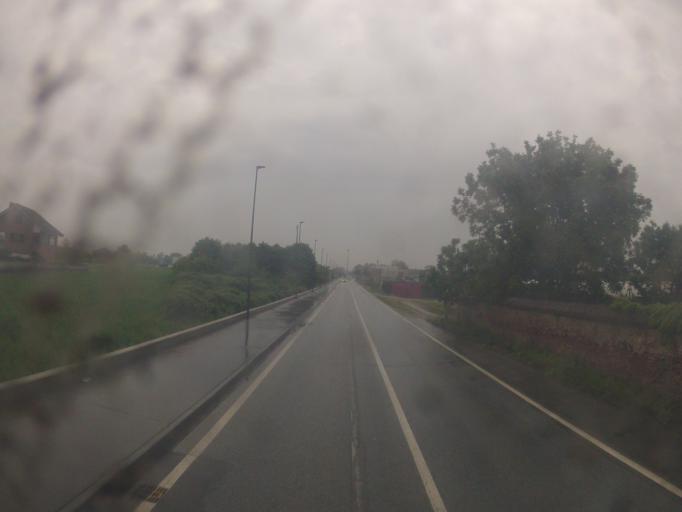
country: IT
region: Piedmont
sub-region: Provincia di Torino
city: La Loggia
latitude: 44.9440
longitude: 7.6700
